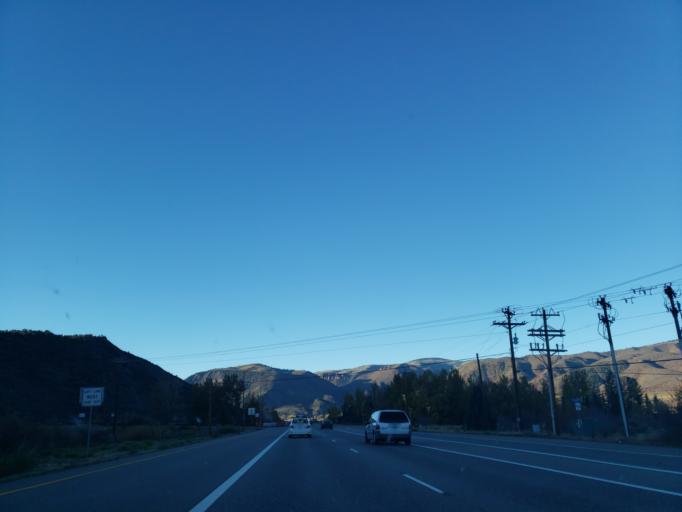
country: US
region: Colorado
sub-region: Pitkin County
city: Snowmass Village
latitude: 39.2599
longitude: -106.8873
